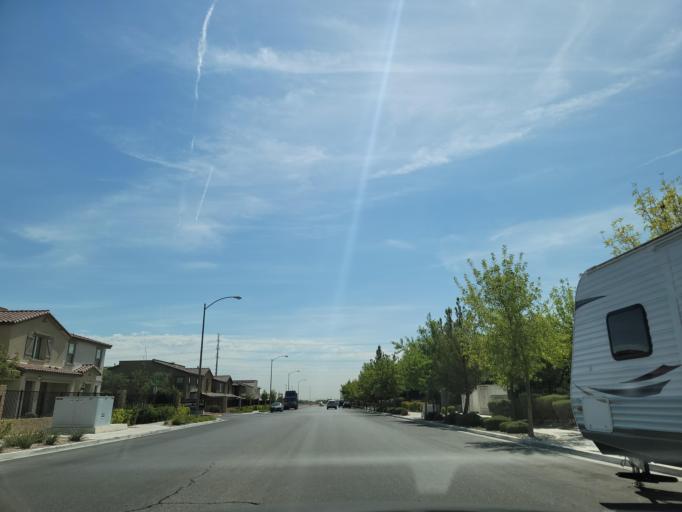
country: US
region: Nevada
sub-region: Clark County
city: Spring Valley
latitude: 36.0740
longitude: -115.2825
